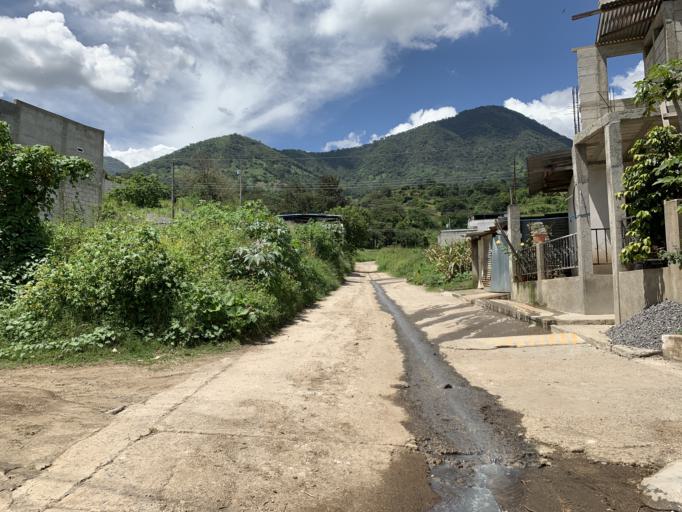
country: GT
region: Guatemala
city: Amatitlan
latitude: 14.4879
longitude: -90.6437
